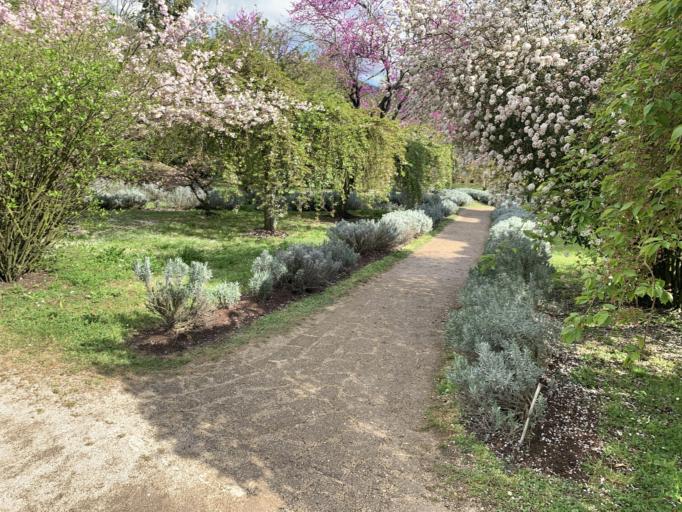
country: IT
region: Latium
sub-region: Provincia di Latina
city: Norma
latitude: 41.5807
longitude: 12.9523
